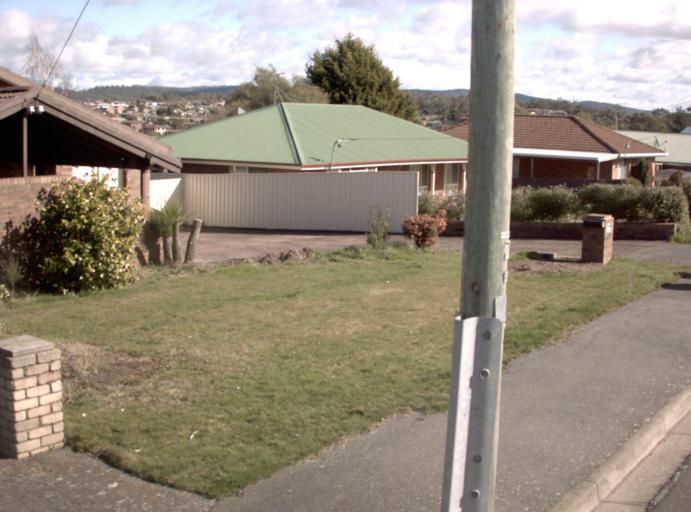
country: AU
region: Tasmania
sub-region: Launceston
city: Summerhill
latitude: -41.4645
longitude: 147.1314
